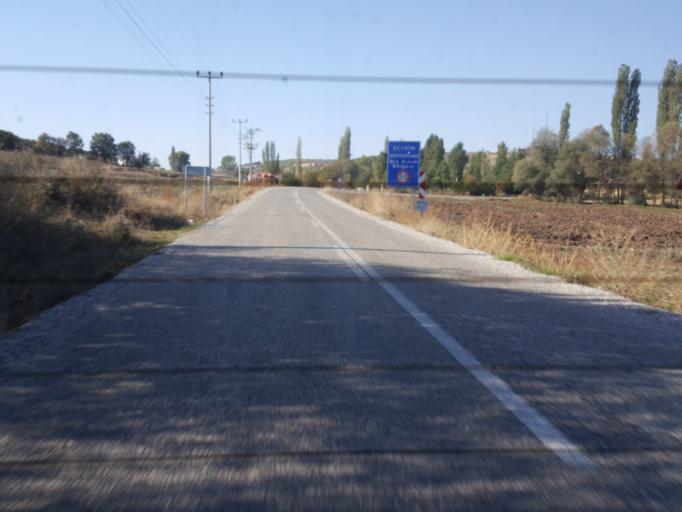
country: TR
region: Corum
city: Seydim
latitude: 40.5464
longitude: 34.7509
